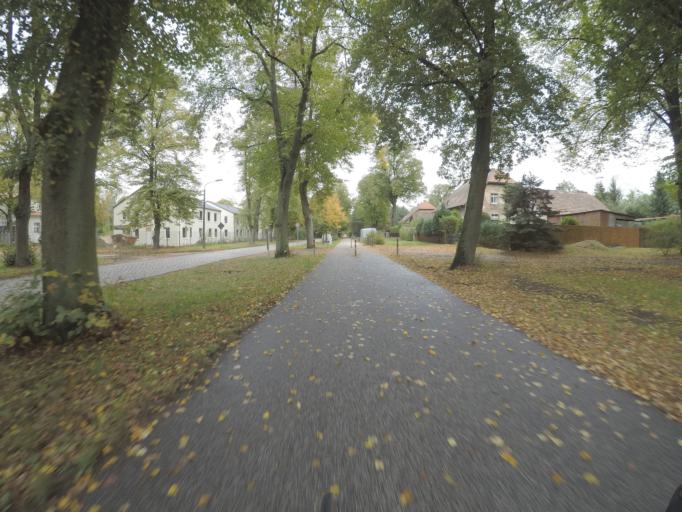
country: DE
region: Berlin
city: Buch
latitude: 52.6678
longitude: 13.4961
